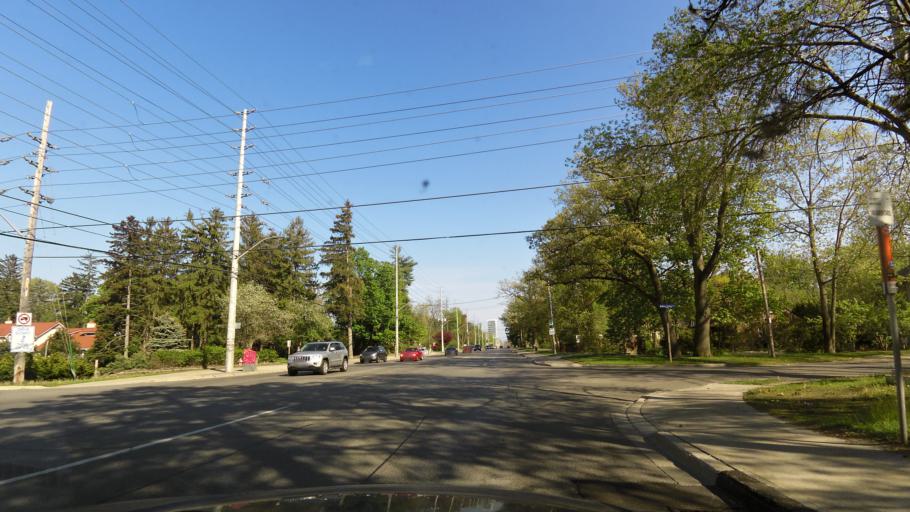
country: CA
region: Ontario
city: Mississauga
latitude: 43.5646
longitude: -79.5949
